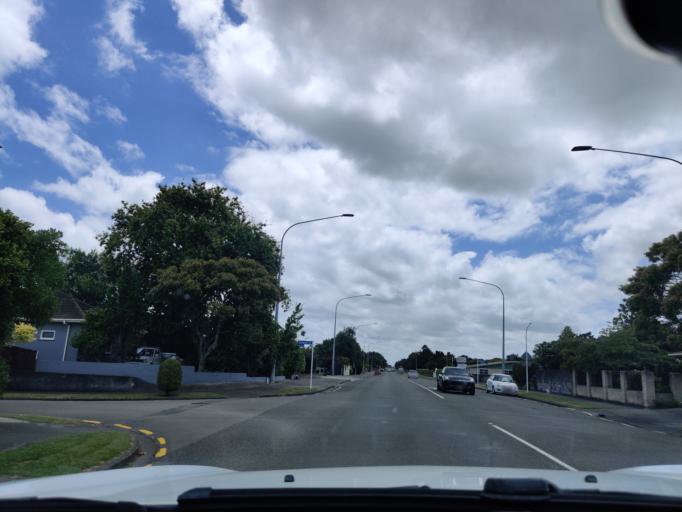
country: NZ
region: Manawatu-Wanganui
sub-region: Palmerston North City
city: Palmerston North
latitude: -40.3601
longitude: 175.6317
